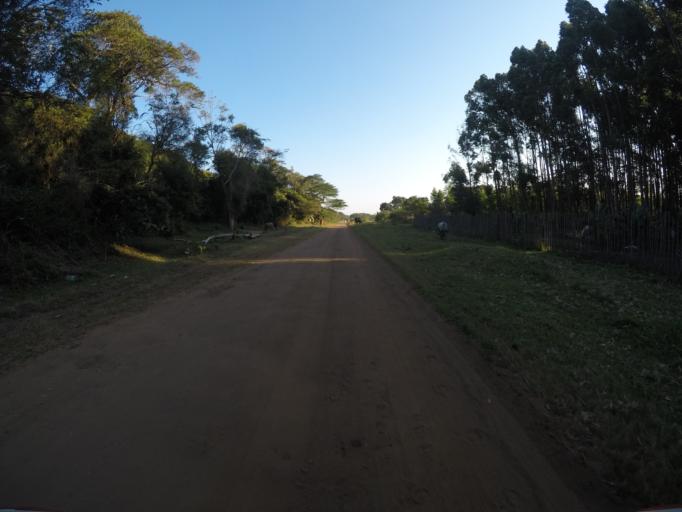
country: ZA
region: KwaZulu-Natal
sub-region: uThungulu District Municipality
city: KwaMbonambi
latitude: -28.6979
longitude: 32.1946
